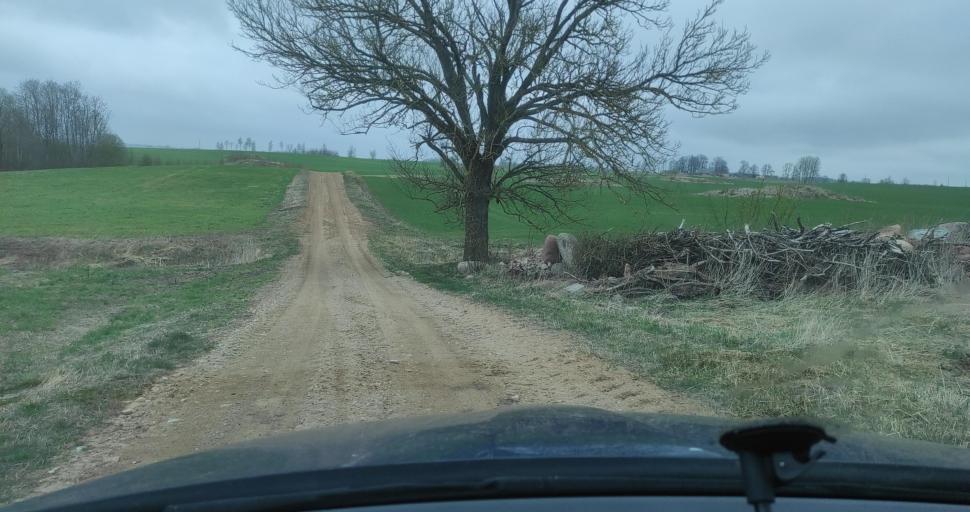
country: LV
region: Broceni
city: Broceni
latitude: 56.7411
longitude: 22.4861
